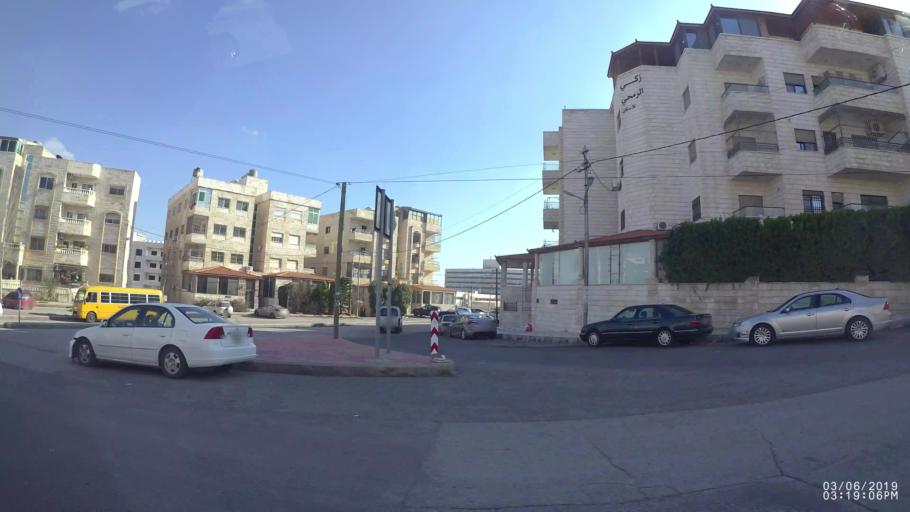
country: JO
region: Amman
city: Amman
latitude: 31.9870
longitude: 35.9384
